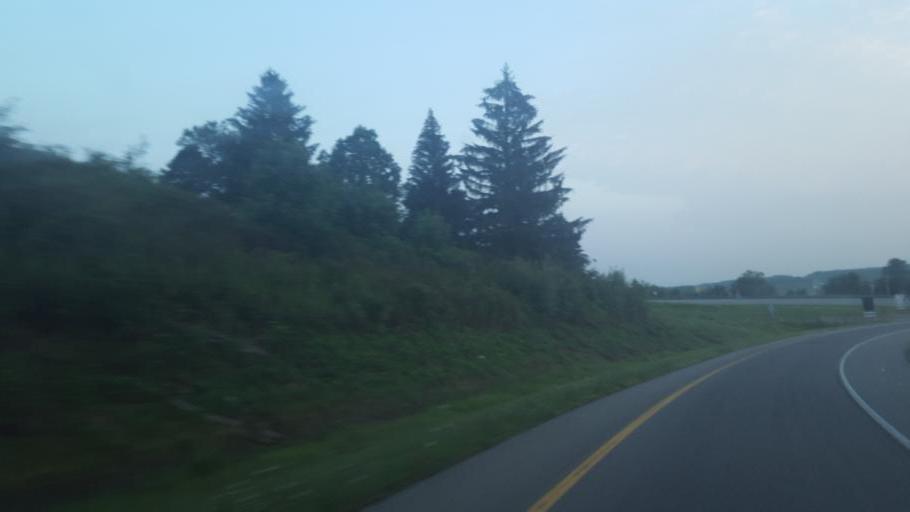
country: US
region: Pennsylvania
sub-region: Crawford County
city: Meadville
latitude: 41.5369
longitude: -80.1811
